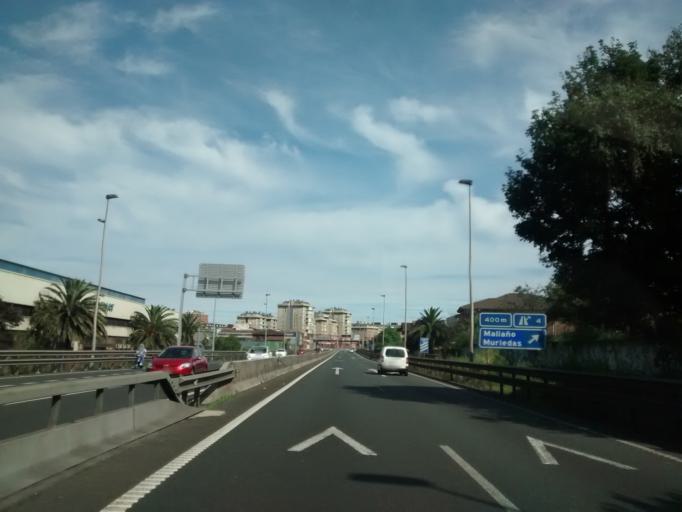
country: ES
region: Cantabria
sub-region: Provincia de Cantabria
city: El Astillero
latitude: 43.4134
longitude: -3.8368
